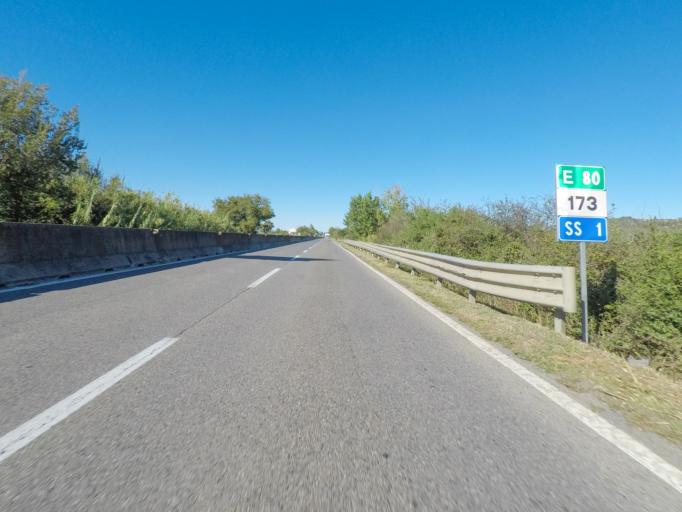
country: IT
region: Tuscany
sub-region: Provincia di Grosseto
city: Grosseto
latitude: 42.6927
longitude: 11.1381
